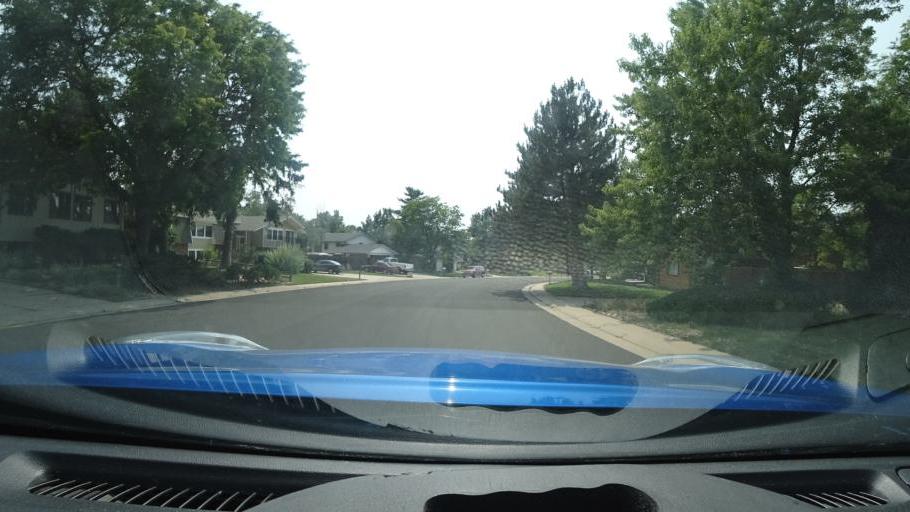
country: US
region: Colorado
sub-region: Adams County
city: Aurora
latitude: 39.6729
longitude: -104.8575
